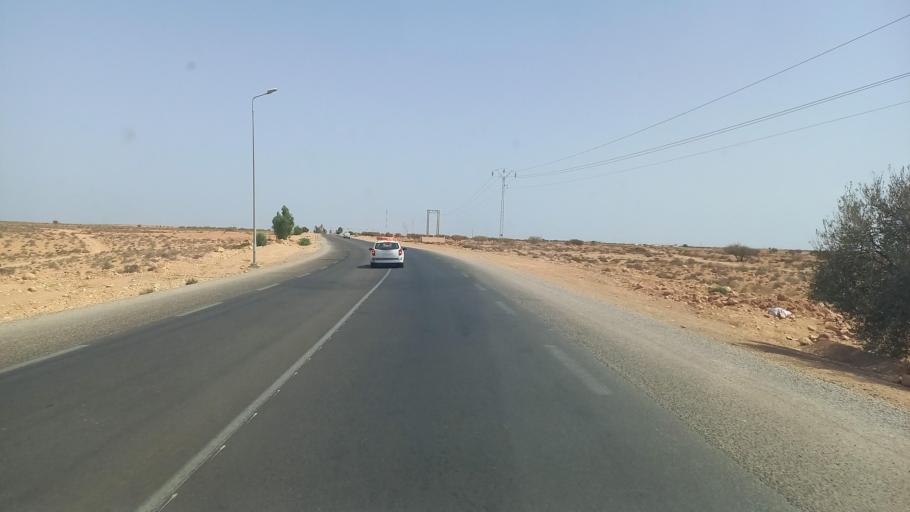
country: TN
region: Madanin
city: Medenine
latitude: 33.3769
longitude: 10.6966
